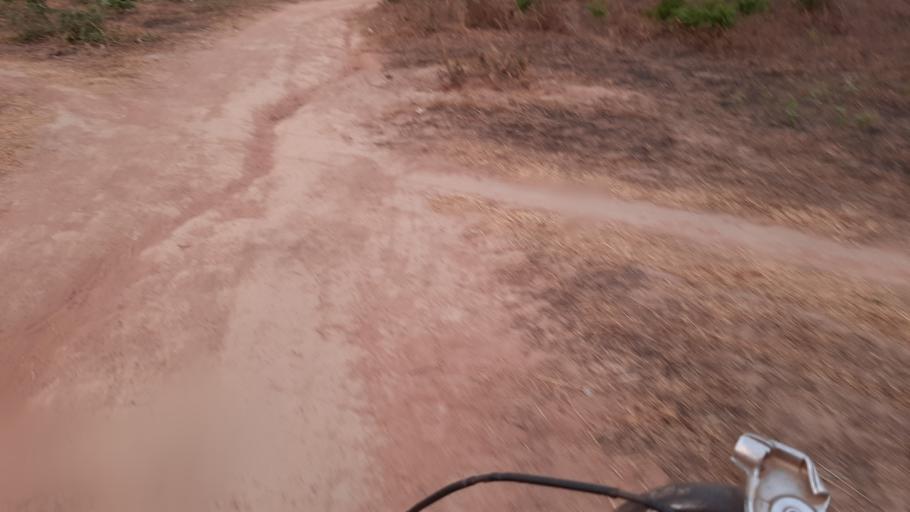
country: GH
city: Kpandae
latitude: 8.8422
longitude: 0.0444
